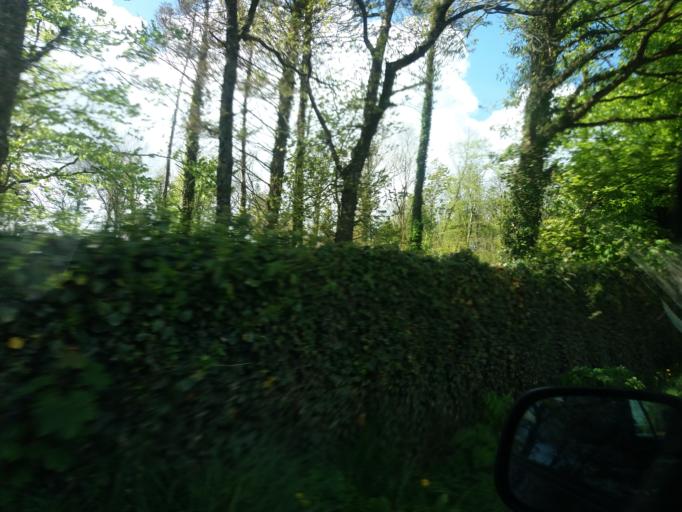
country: IE
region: Munster
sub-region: Waterford
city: Dunmore East
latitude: 52.2409
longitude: -6.9348
